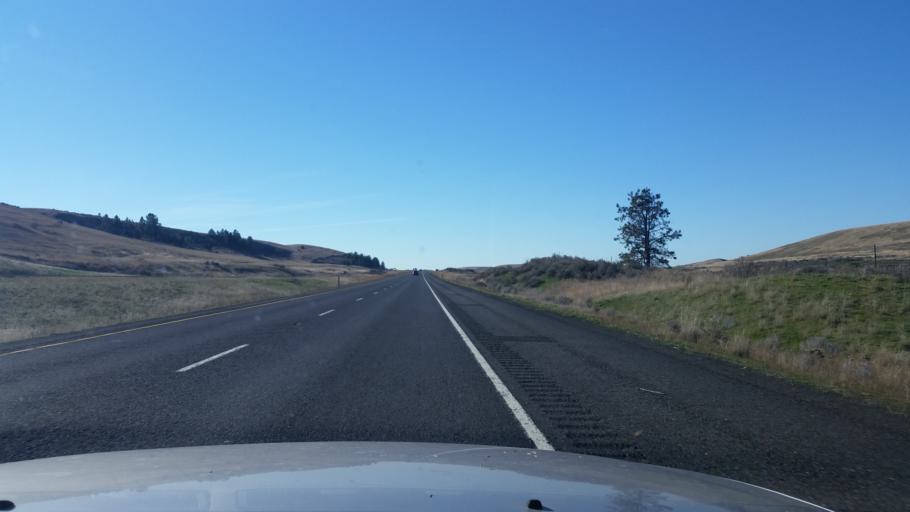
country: US
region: Washington
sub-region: Spokane County
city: Medical Lake
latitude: 47.3785
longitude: -117.8689
